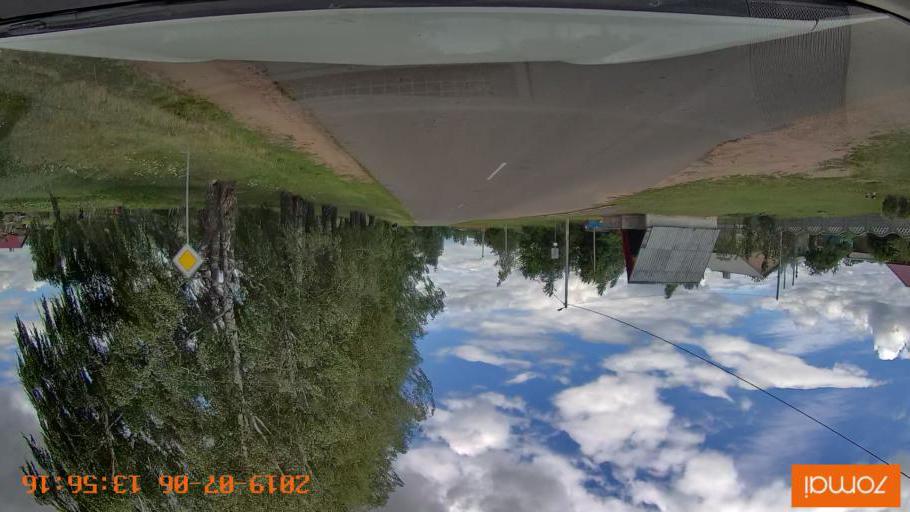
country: BY
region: Minsk
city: Ivyanyets
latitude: 53.7638
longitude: 26.8038
